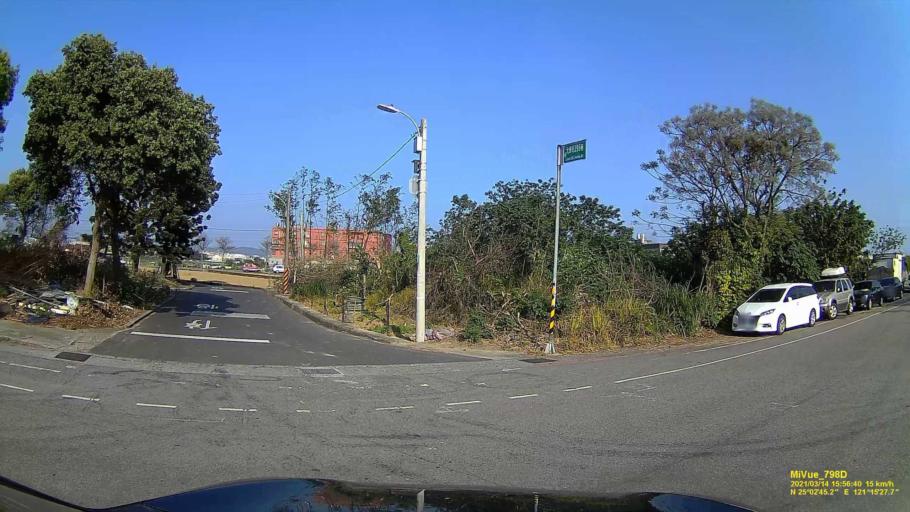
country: TW
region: Taiwan
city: Taoyuan City
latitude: 25.0459
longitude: 121.2578
